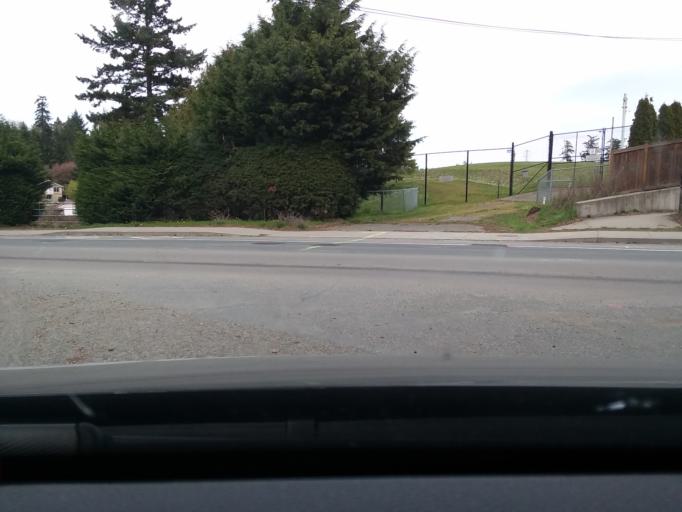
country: CA
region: British Columbia
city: Victoria
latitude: 48.4820
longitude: -123.4134
